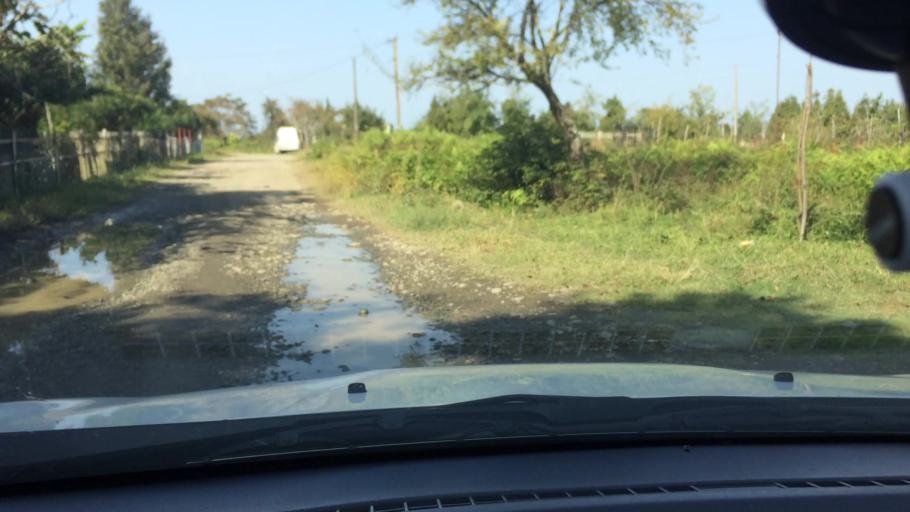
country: GE
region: Ajaria
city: Kobuleti
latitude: 41.8093
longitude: 41.8209
